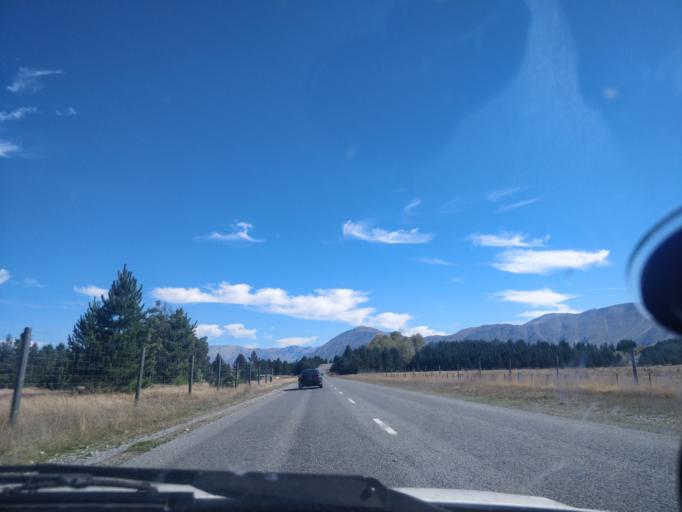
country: NZ
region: Otago
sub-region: Queenstown-Lakes District
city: Wanaka
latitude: -44.2723
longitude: 170.0545
